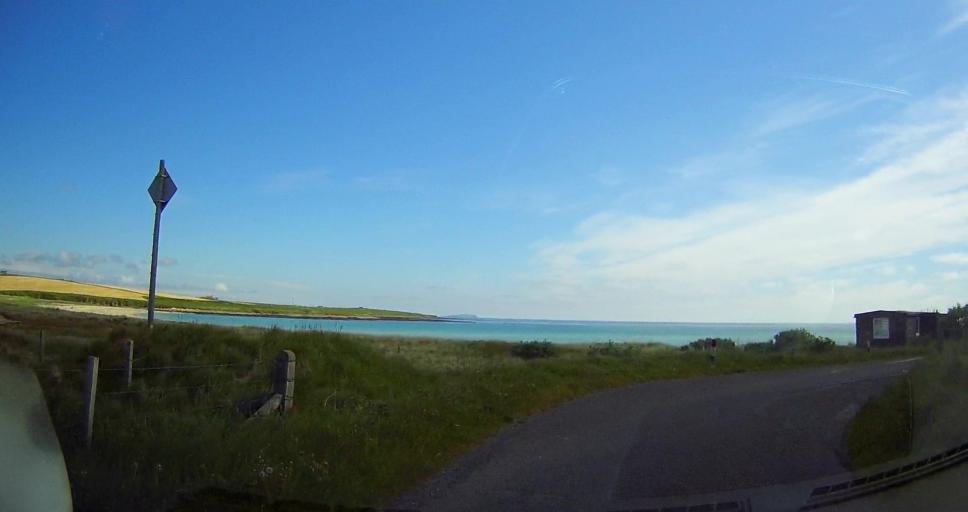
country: GB
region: Scotland
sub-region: Orkney Islands
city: Kirkwall
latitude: 58.8372
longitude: -2.9049
